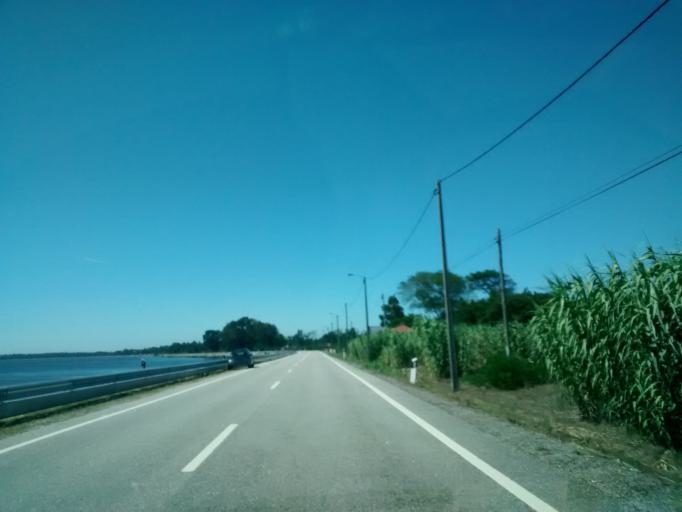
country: PT
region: Aveiro
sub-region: Murtosa
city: Murtosa
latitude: 40.7154
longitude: -8.7040
